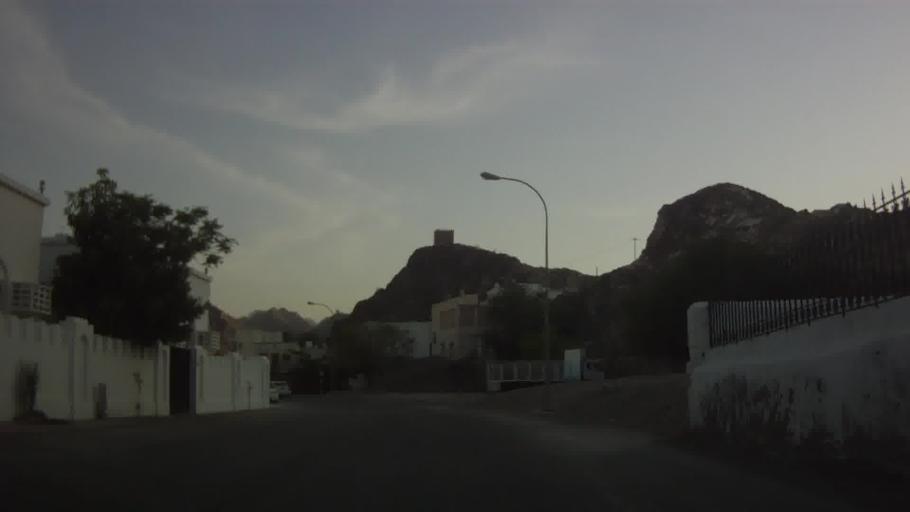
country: OM
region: Muhafazat Masqat
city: Muscat
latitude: 23.6148
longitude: 58.5887
